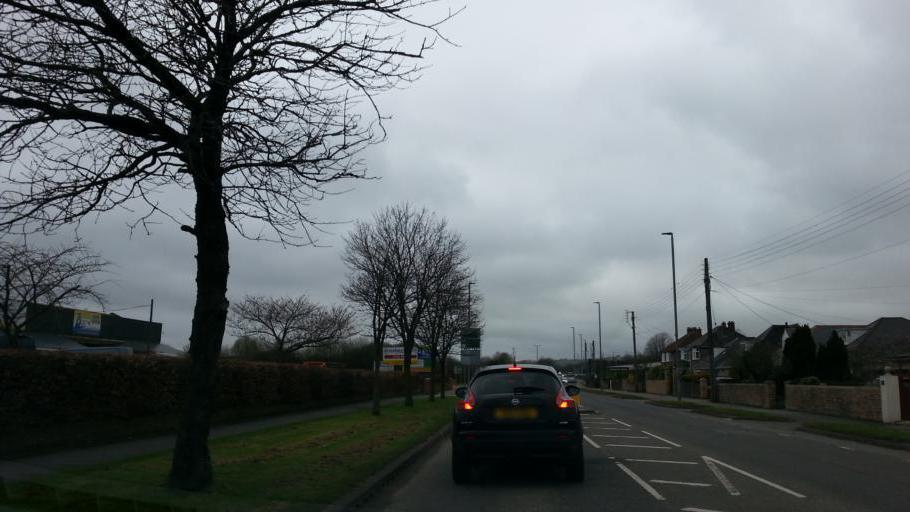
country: GB
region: England
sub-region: Devon
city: Barnstaple
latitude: 51.0849
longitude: -4.0704
